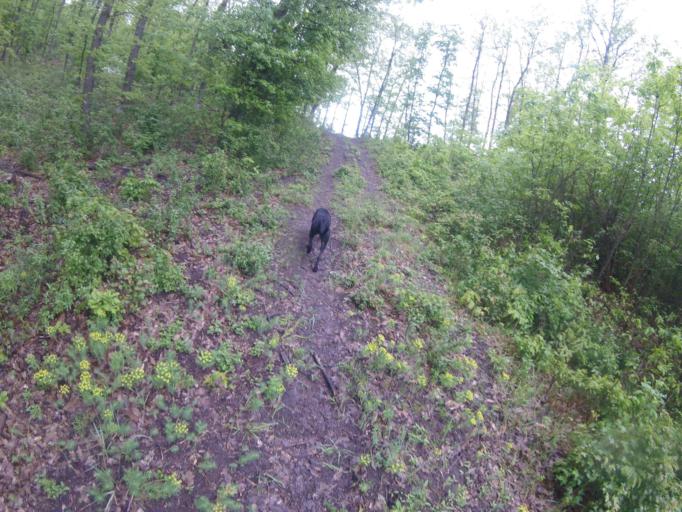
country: HU
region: Nograd
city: Matraverebely
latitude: 47.9968
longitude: 19.7546
